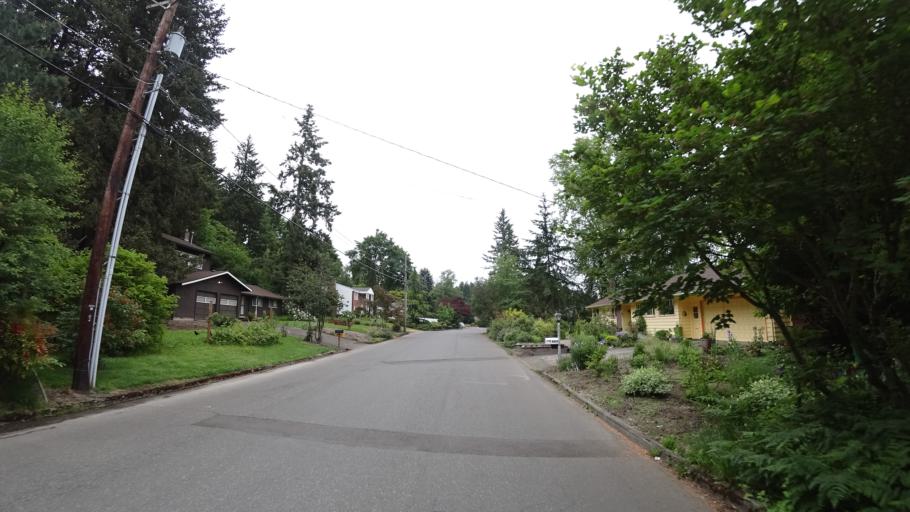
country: US
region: Oregon
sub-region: Washington County
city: Garden Home-Whitford
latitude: 45.4629
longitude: -122.7357
